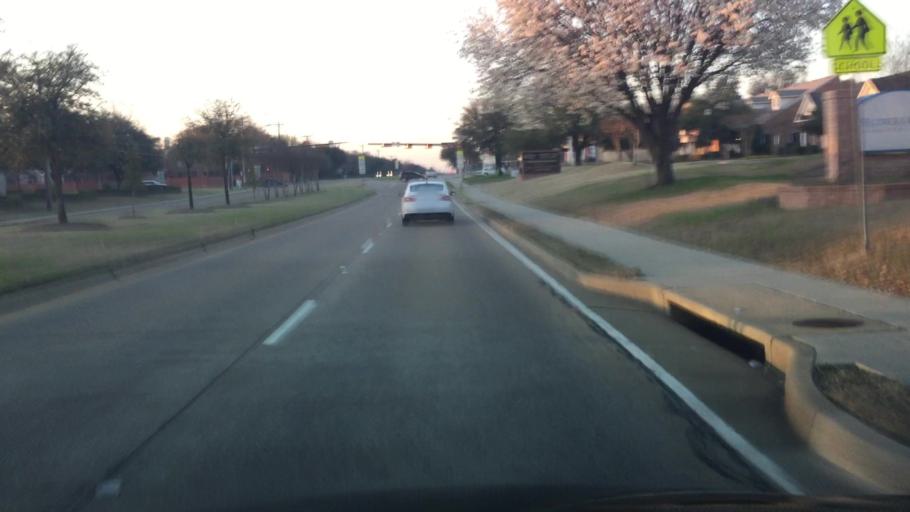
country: US
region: Texas
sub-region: Denton County
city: Highland Village
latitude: 33.0677
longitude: -97.0619
